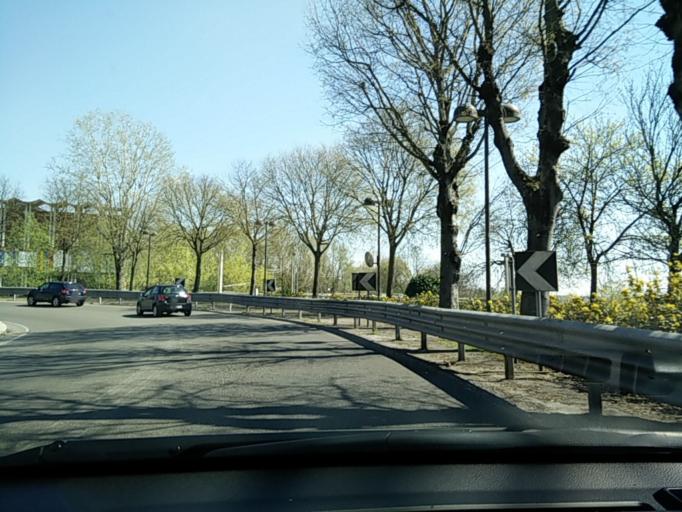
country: IT
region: Lombardy
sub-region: Provincia di Pavia
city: Pavia
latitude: 45.1779
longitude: 9.1650
